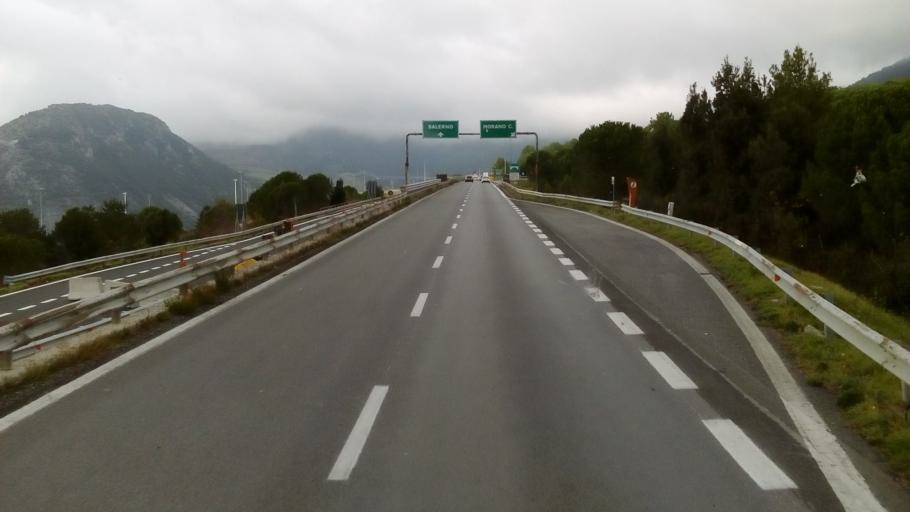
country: IT
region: Calabria
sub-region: Provincia di Cosenza
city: Morano Calabro
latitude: 39.8718
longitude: 16.1729
